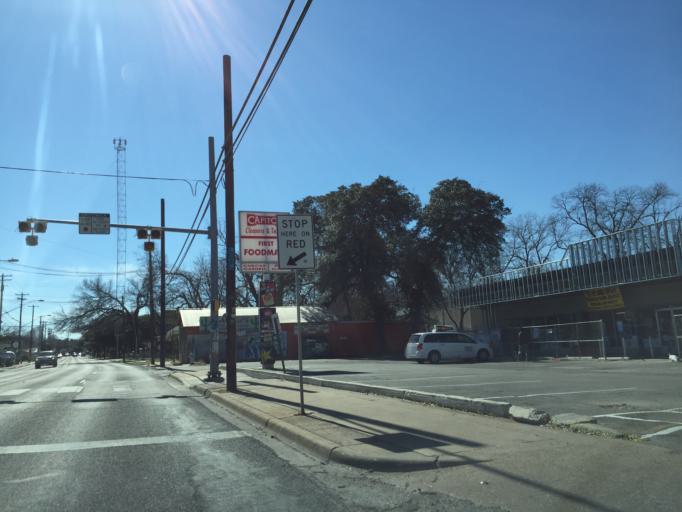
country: US
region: Texas
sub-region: Travis County
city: Austin
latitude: 30.2507
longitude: -97.7547
